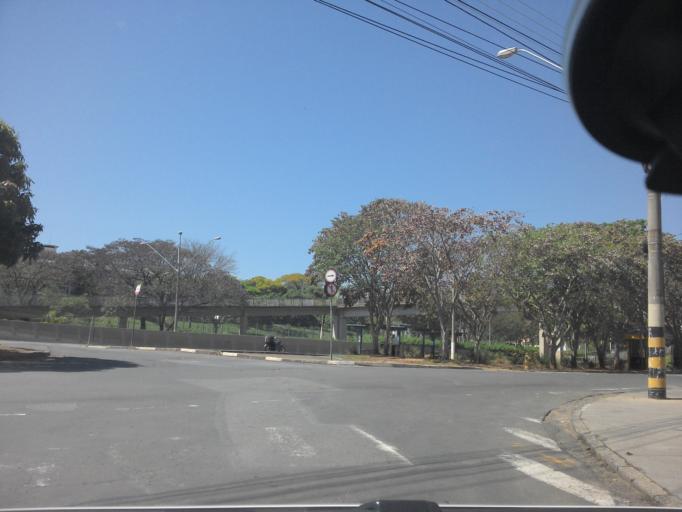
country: BR
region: Sao Paulo
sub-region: Campinas
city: Campinas
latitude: -22.8492
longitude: -47.0426
